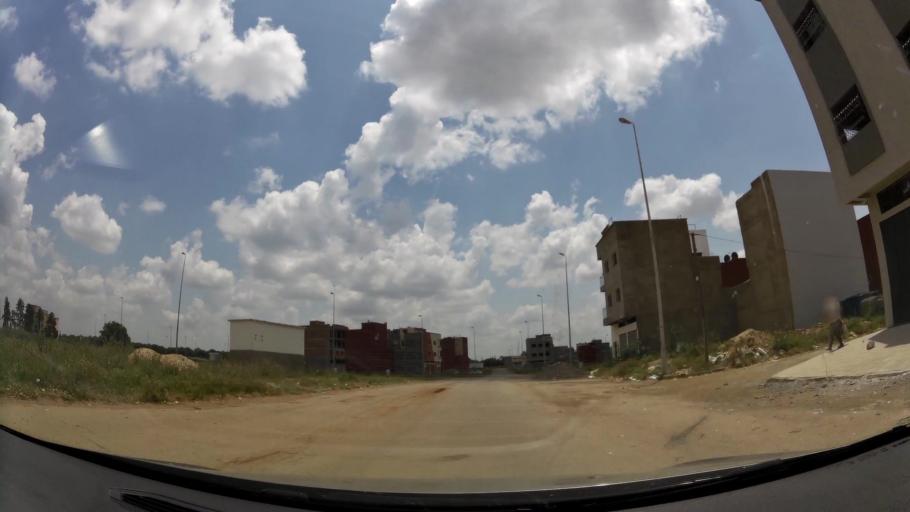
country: MA
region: Rabat-Sale-Zemmour-Zaer
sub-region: Khemisset
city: Tiflet
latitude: 34.0006
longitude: -6.5233
